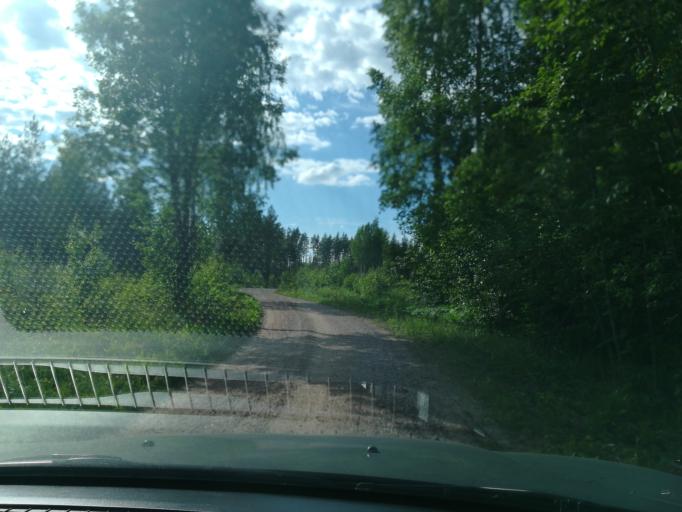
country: FI
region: Southern Savonia
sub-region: Savonlinna
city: Savonlinna
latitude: 61.6418
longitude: 28.7198
